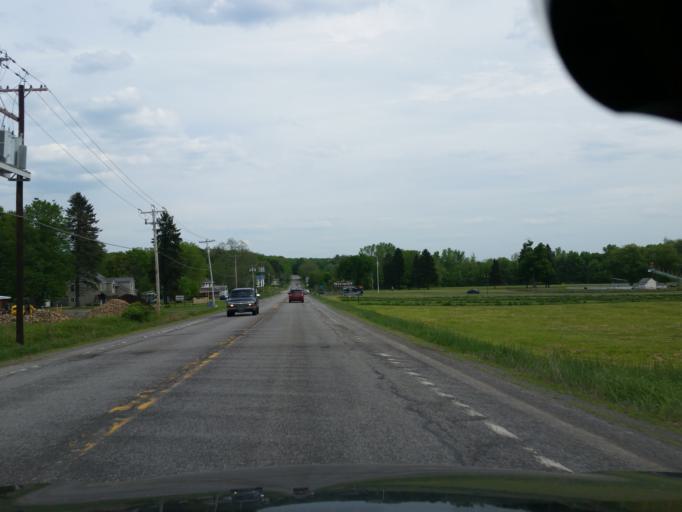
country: US
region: New York
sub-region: Chautauqua County
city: Mayville
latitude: 42.2041
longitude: -79.4216
